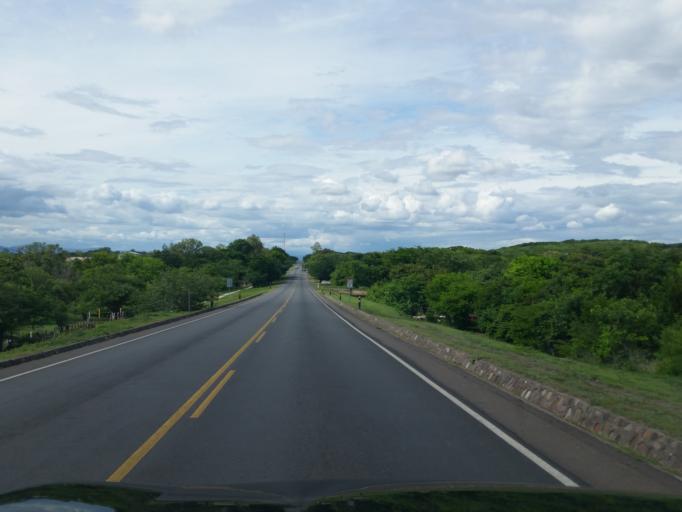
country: NI
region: Matagalpa
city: Ciudad Dario
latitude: 12.7694
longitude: -86.1246
